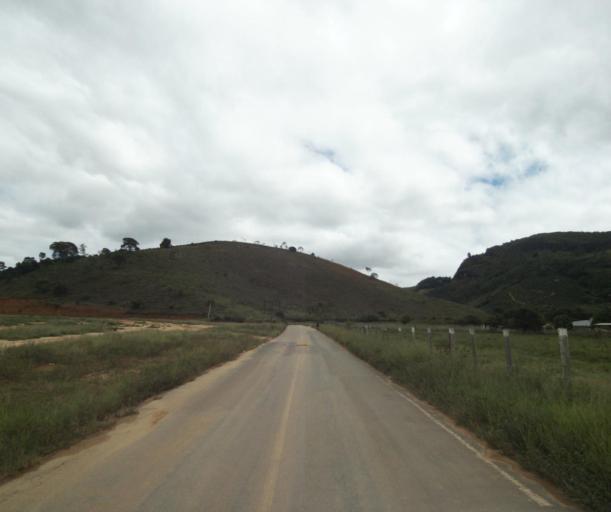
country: BR
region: Espirito Santo
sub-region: Irupi
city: Irupi
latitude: -20.3379
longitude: -41.6456
